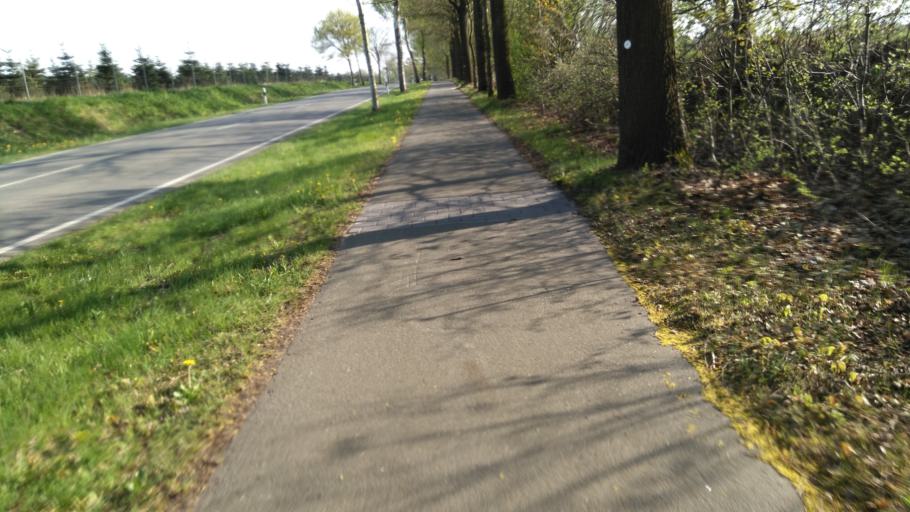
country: DE
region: Lower Saxony
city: Buxtehude
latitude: 53.4456
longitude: 9.6934
